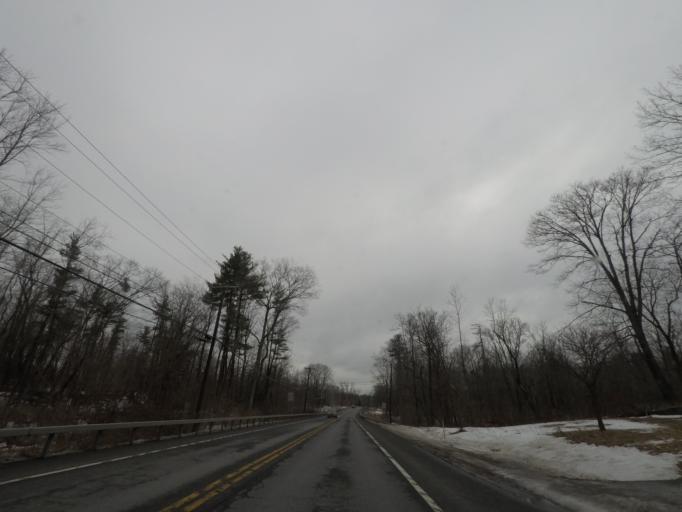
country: US
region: New York
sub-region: Albany County
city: Voorheesville
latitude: 42.6602
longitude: -73.9150
